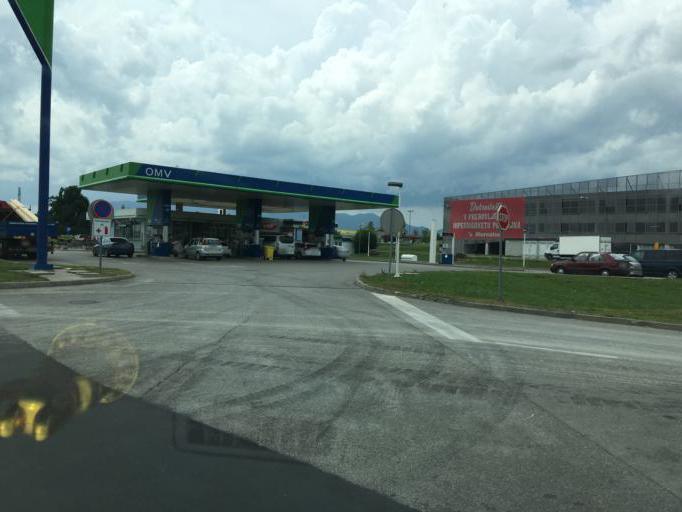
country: SI
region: Postojna
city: Postojna
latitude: 45.7710
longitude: 14.2019
